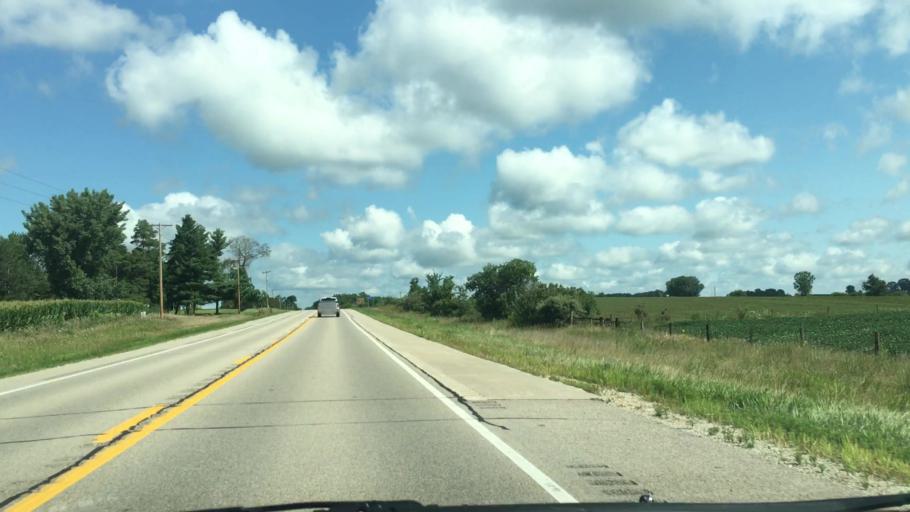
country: US
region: Iowa
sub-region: Johnson County
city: Solon
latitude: 41.8274
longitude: -91.4977
